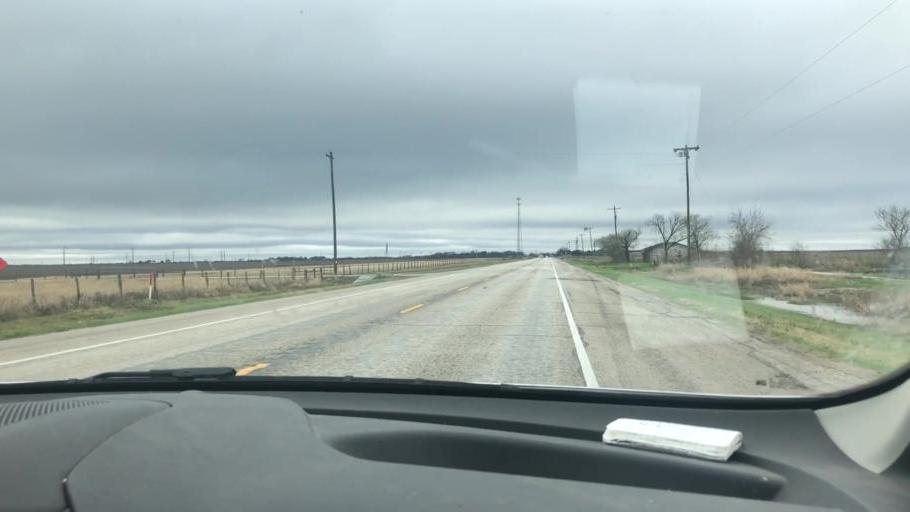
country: US
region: Texas
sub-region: Wharton County
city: Wharton
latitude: 29.2396
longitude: -96.0400
